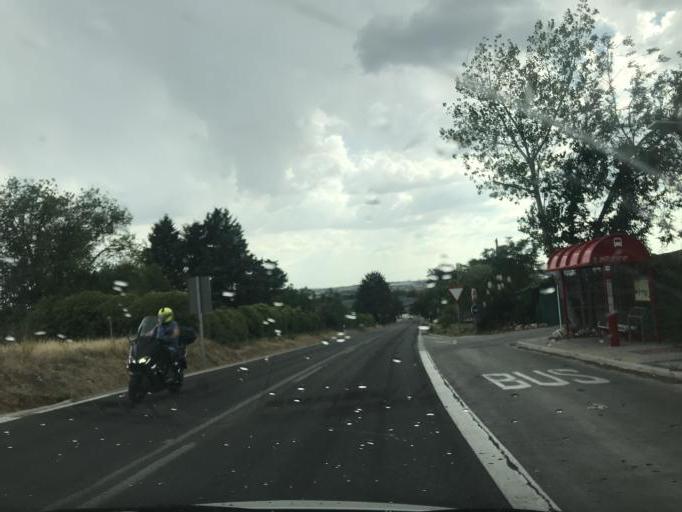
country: ES
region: Madrid
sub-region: Provincia de Madrid
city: Paracuellos de Jarama
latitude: 40.5018
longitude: -3.5418
